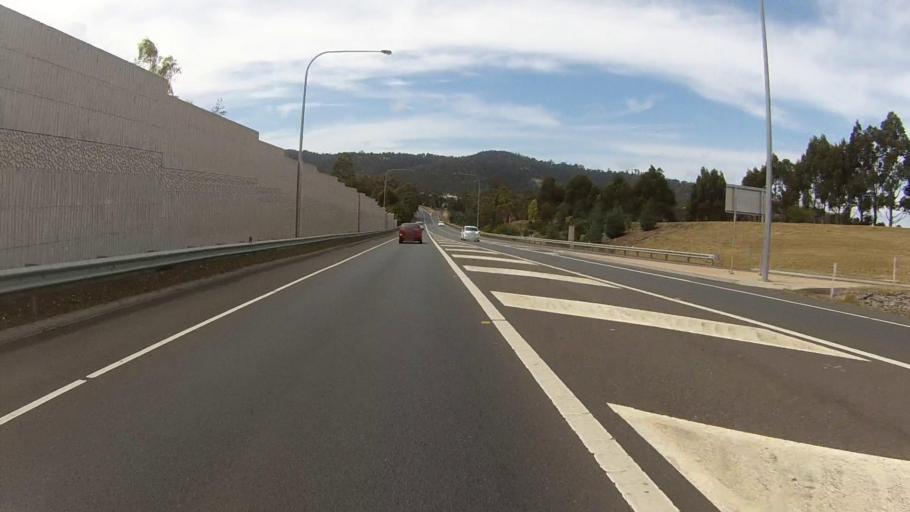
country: AU
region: Tasmania
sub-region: Kingborough
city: Kingston
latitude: -42.9738
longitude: 147.3046
